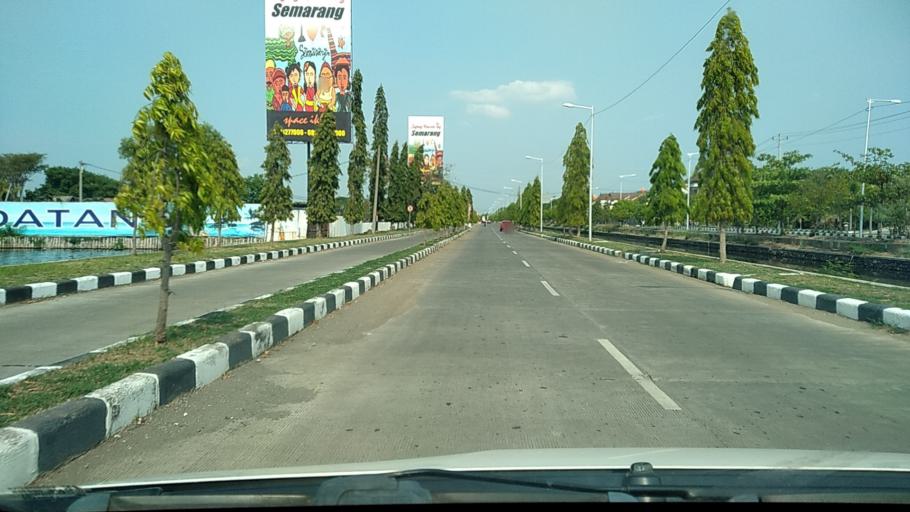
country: ID
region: Central Java
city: Semarang
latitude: -6.9630
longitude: 110.3849
